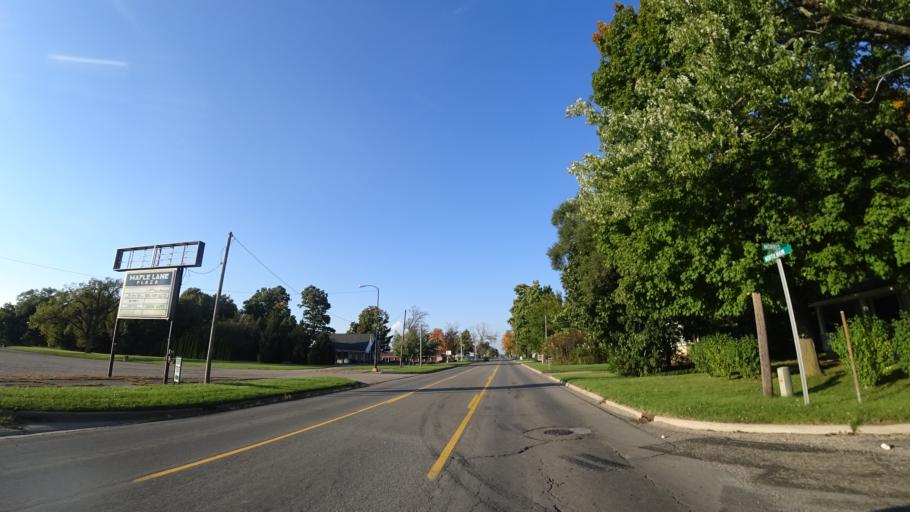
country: US
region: Michigan
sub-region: Saint Joseph County
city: Three Rivers
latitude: 41.9590
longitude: -85.6347
